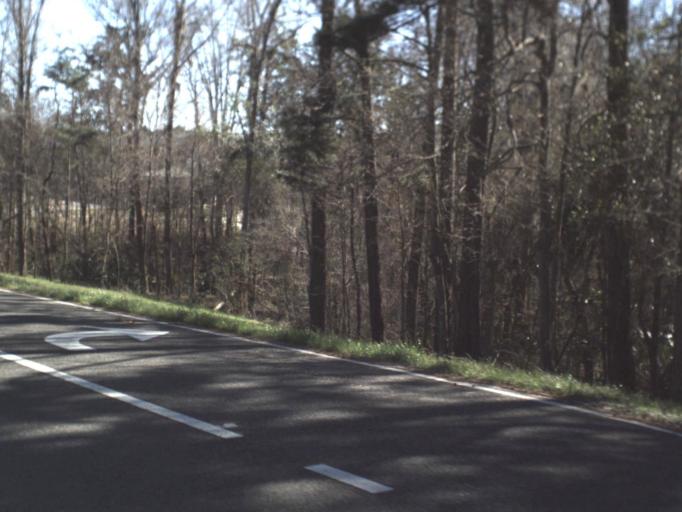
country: US
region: Florida
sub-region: Gadsden County
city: Midway
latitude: 30.5486
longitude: -84.4871
